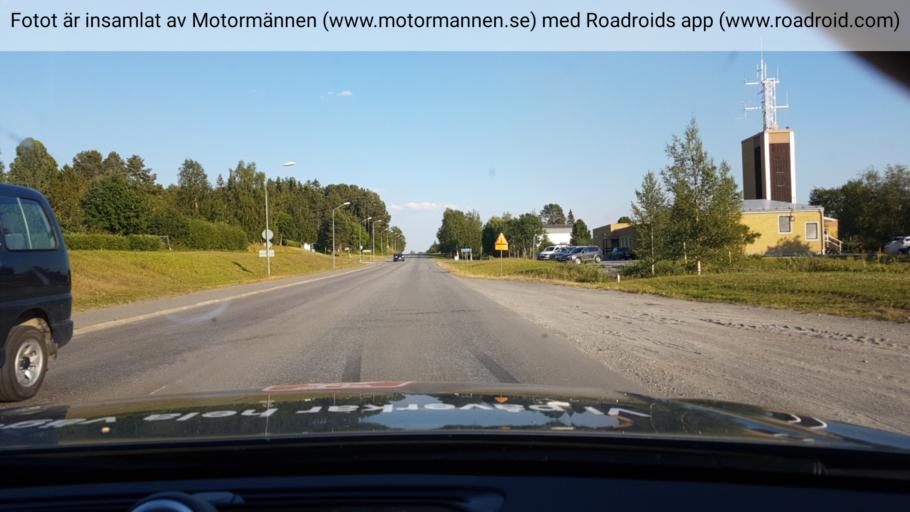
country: SE
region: Jaemtland
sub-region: Are Kommun
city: Jarpen
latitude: 63.3505
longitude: 13.4508
